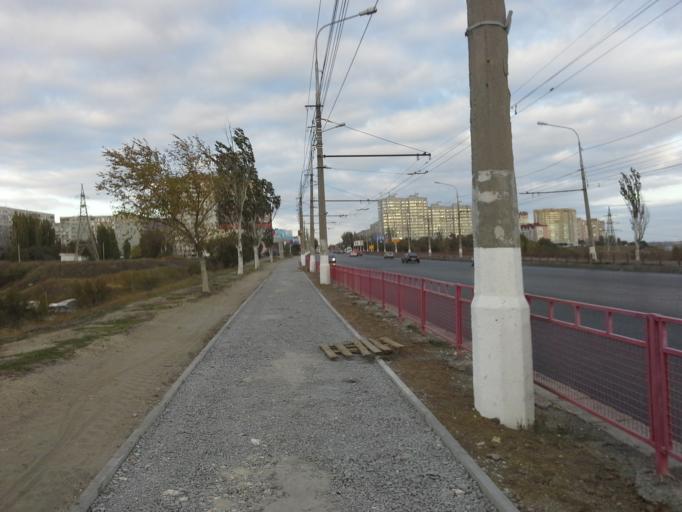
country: RU
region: Volgograd
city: Vodstroy
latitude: 48.8117
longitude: 44.6158
